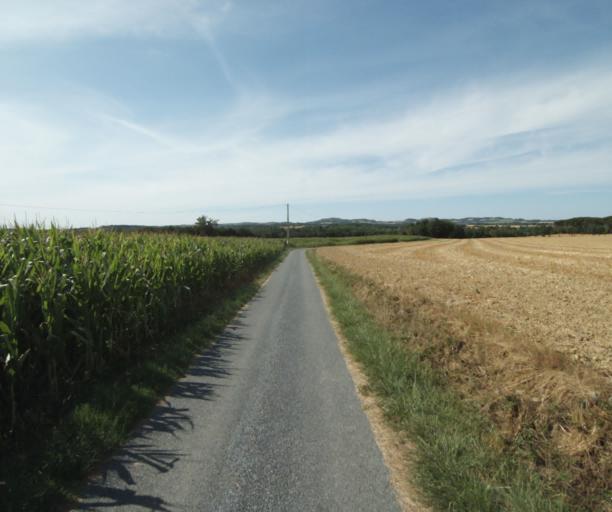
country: FR
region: Midi-Pyrenees
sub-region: Departement du Tarn
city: Soual
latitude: 43.5150
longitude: 2.0882
